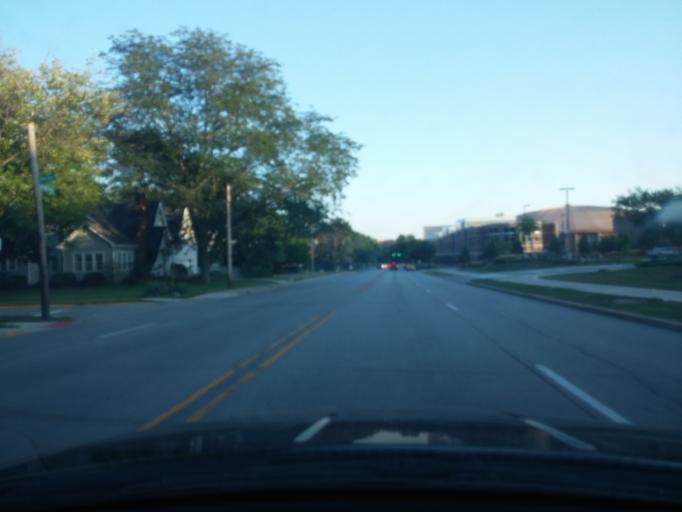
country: US
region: Indiana
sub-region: Tippecanoe County
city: West Lafayette
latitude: 40.4359
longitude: -86.9154
